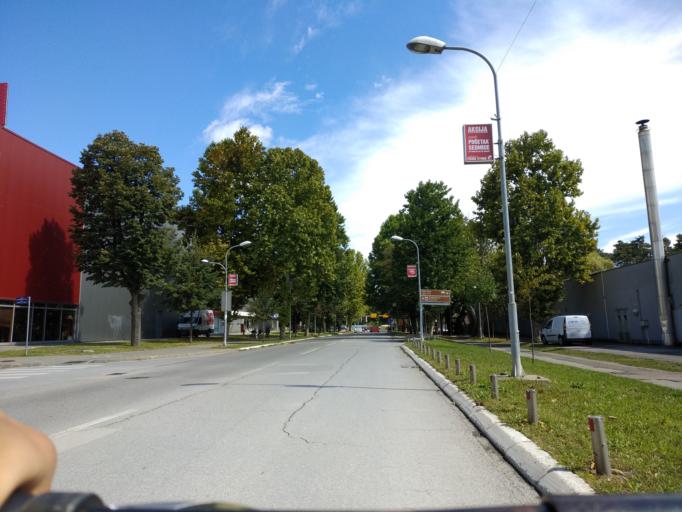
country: BA
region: Republika Srpska
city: Starcevica
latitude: 44.7745
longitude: 17.2051
